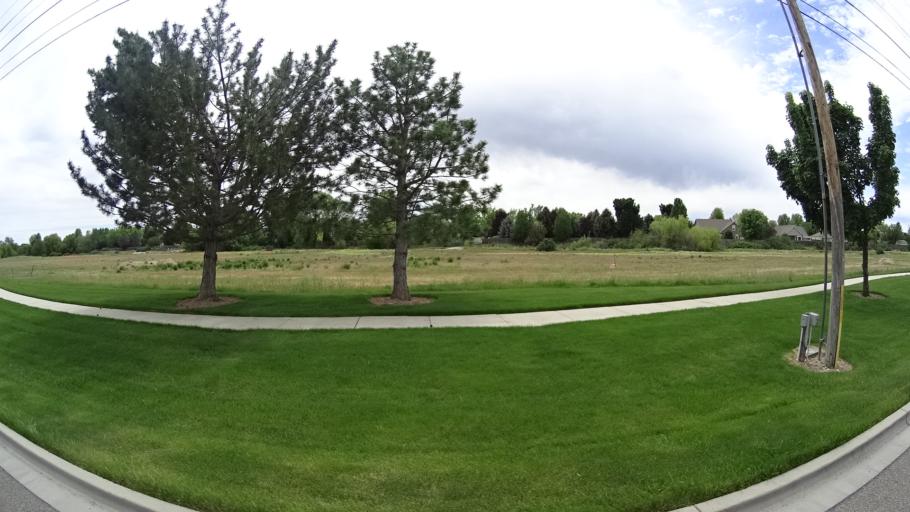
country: US
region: Idaho
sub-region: Ada County
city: Meridian
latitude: 43.5904
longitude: -116.3210
